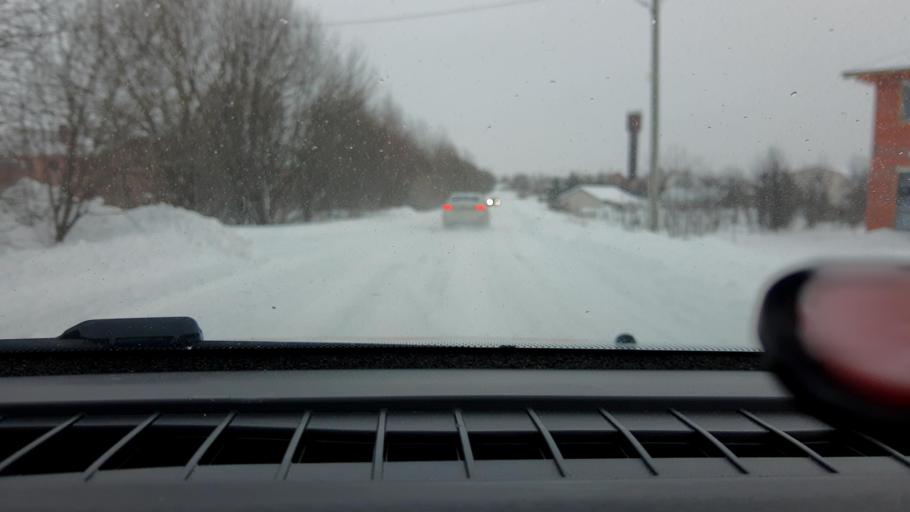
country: RU
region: Nizjnij Novgorod
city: Burevestnik
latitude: 56.1495
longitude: 43.7636
